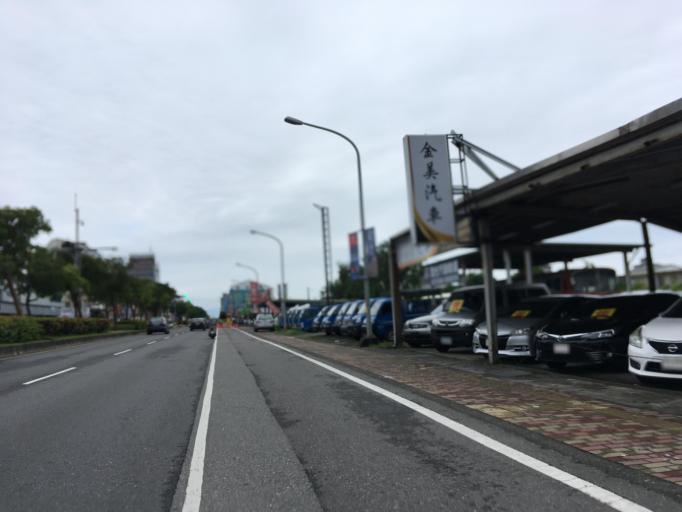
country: TW
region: Taiwan
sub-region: Yilan
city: Yilan
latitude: 24.6999
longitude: 121.7692
